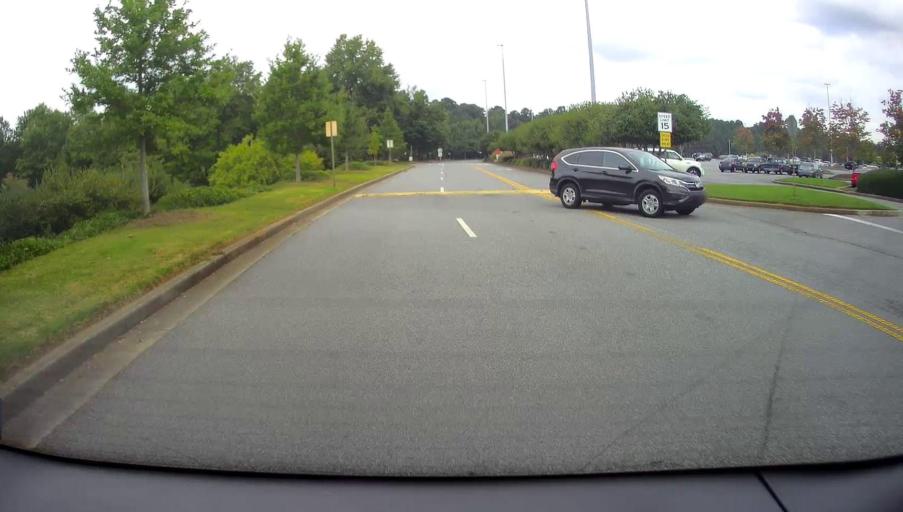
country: US
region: Georgia
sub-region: Fulton County
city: Alpharetta
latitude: 34.0470
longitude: -84.2983
